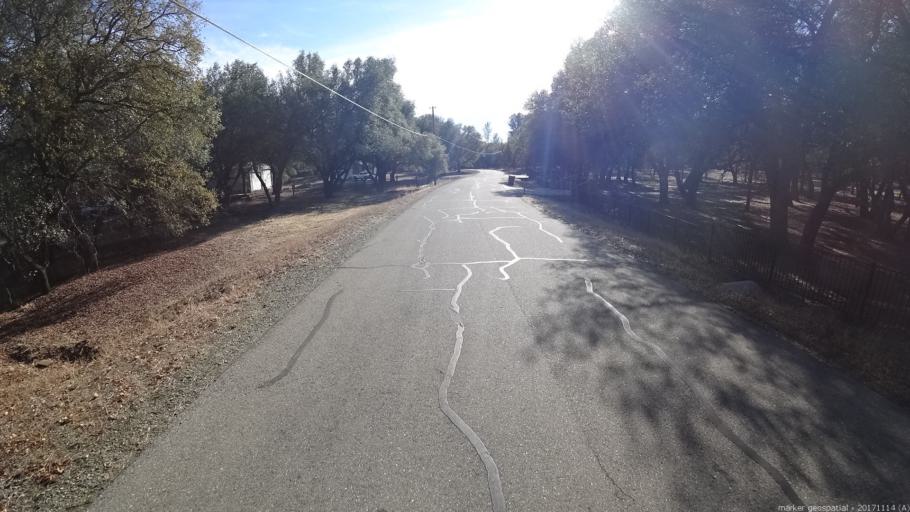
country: US
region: California
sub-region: Shasta County
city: Anderson
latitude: 40.3862
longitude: -122.4471
